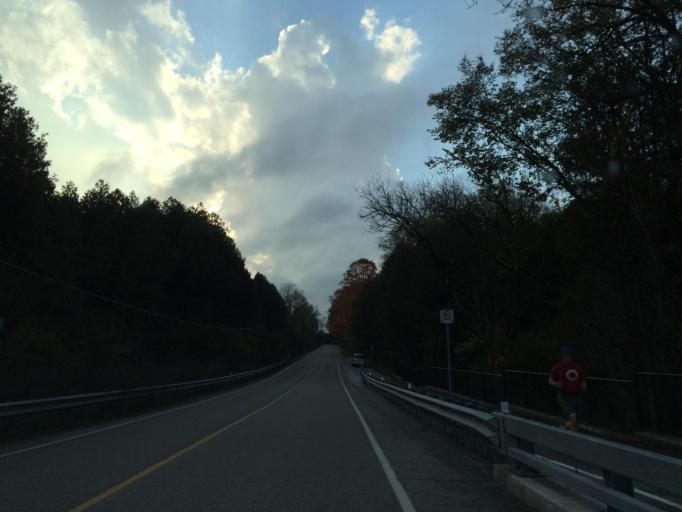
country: CA
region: Ontario
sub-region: Wellington County
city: Guelph
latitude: 43.5024
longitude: -80.2541
